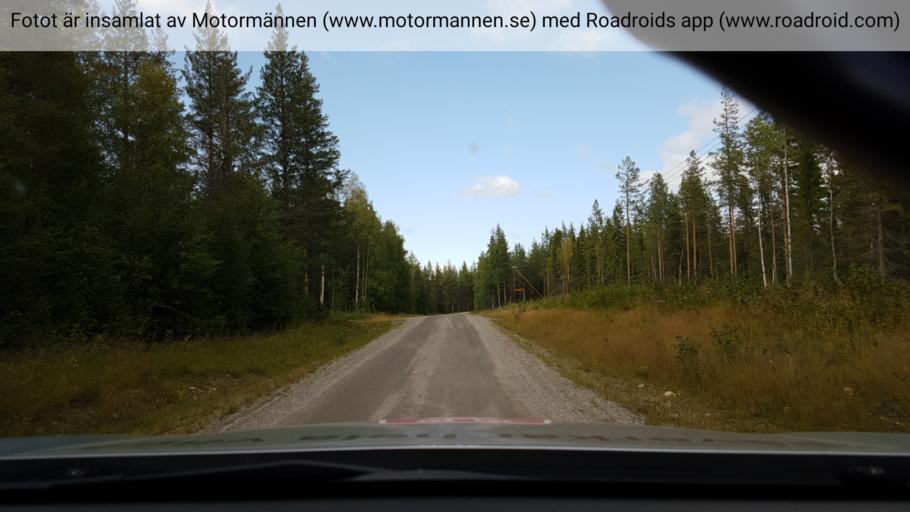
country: SE
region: Vaesterbotten
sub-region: Lycksele Kommun
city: Lycksele
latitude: 64.5442
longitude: 18.9989
